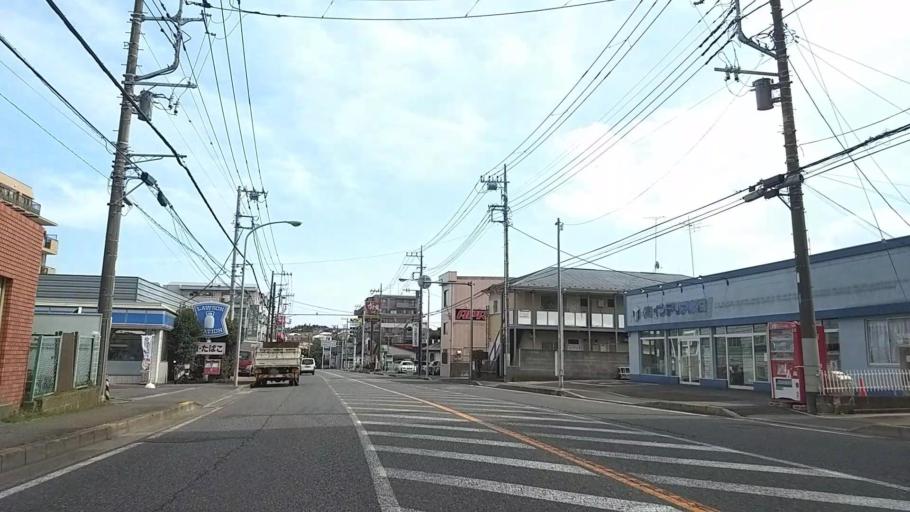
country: JP
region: Kanagawa
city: Yokohama
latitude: 35.5104
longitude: 139.5855
